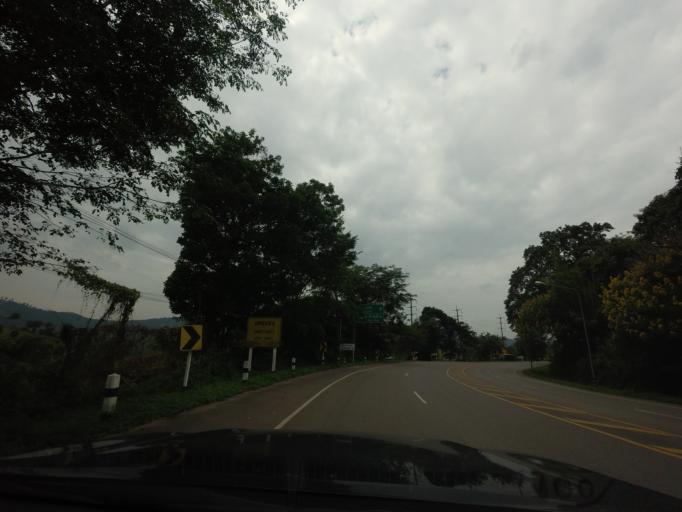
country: TH
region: Loei
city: Dan Sai
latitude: 17.2027
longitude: 101.1601
